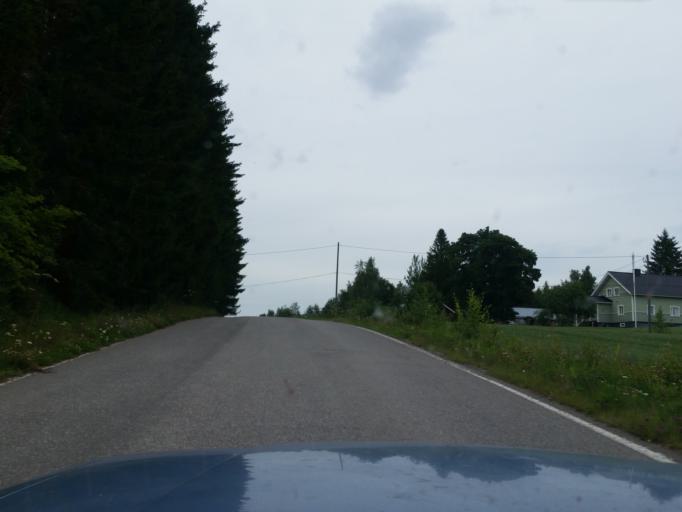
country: FI
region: Uusimaa
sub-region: Helsinki
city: Sammatti
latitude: 60.4622
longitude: 23.8487
